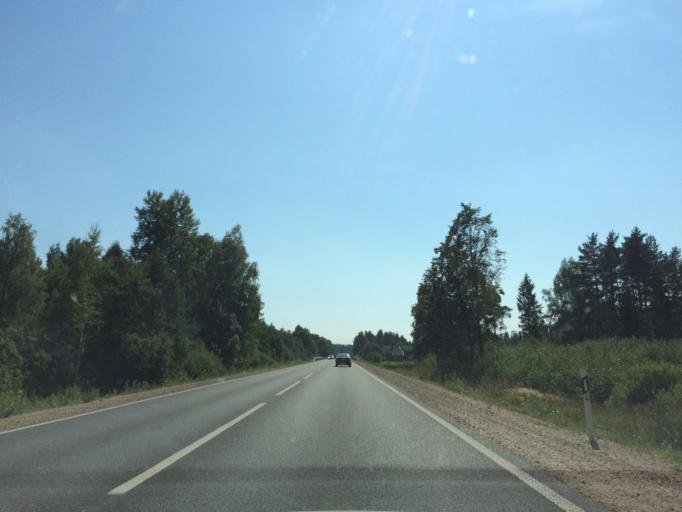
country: LV
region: Rezekne
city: Rezekne
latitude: 56.3605
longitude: 27.1772
